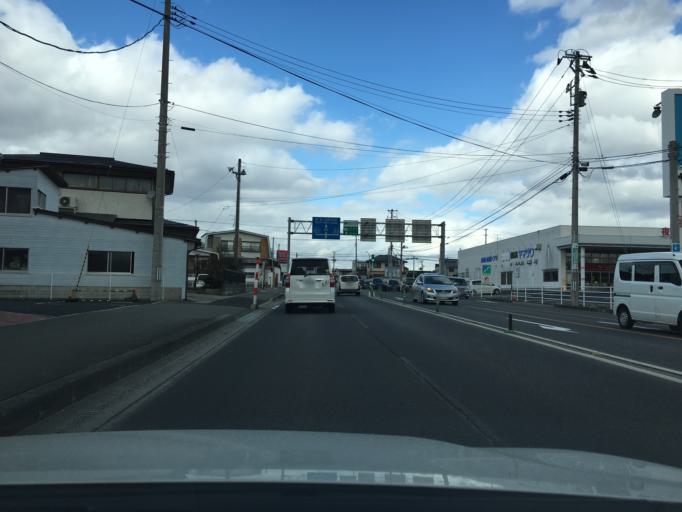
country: JP
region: Yamagata
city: Yamagata-shi
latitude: 38.2319
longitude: 140.3050
